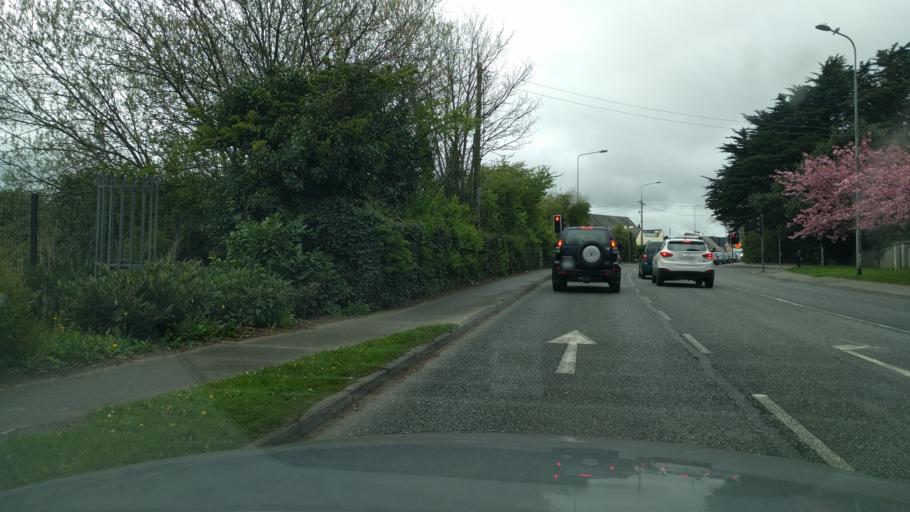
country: IE
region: Leinster
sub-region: Lu
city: Drogheda
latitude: 53.7061
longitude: -6.3724
